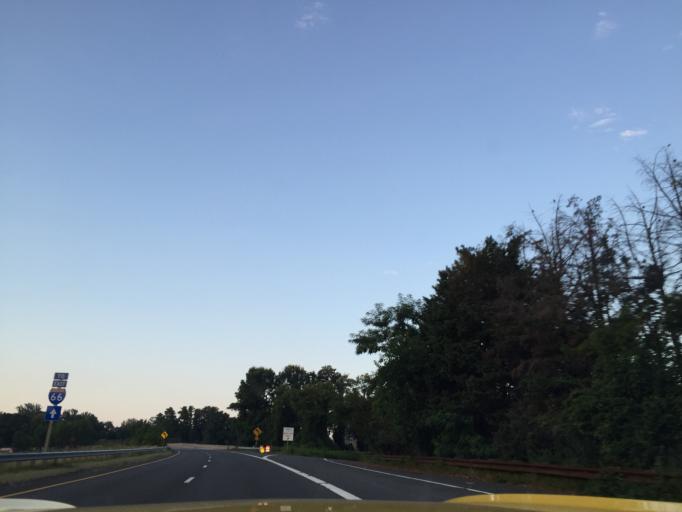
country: US
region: Virginia
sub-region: Fairfax County
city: Pimmit Hills
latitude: 38.9032
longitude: -77.1885
